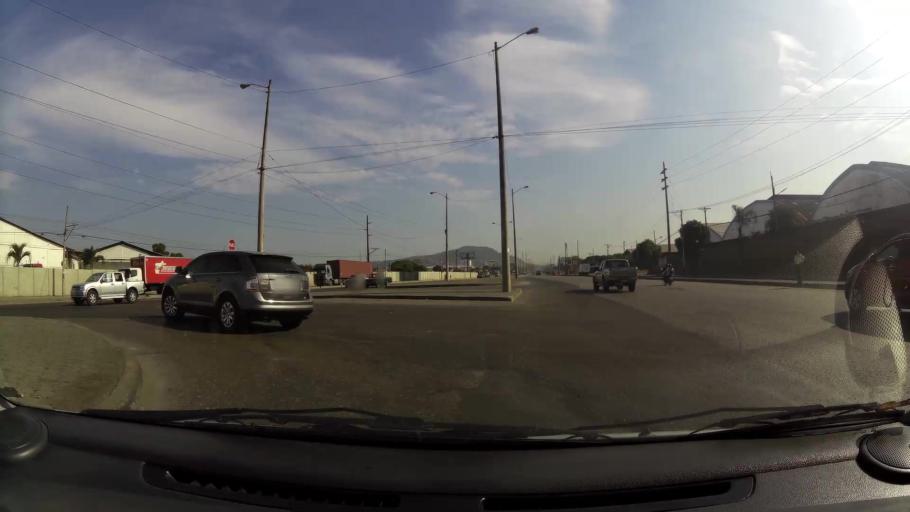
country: EC
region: Guayas
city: Santa Lucia
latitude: -2.0693
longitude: -79.9422
